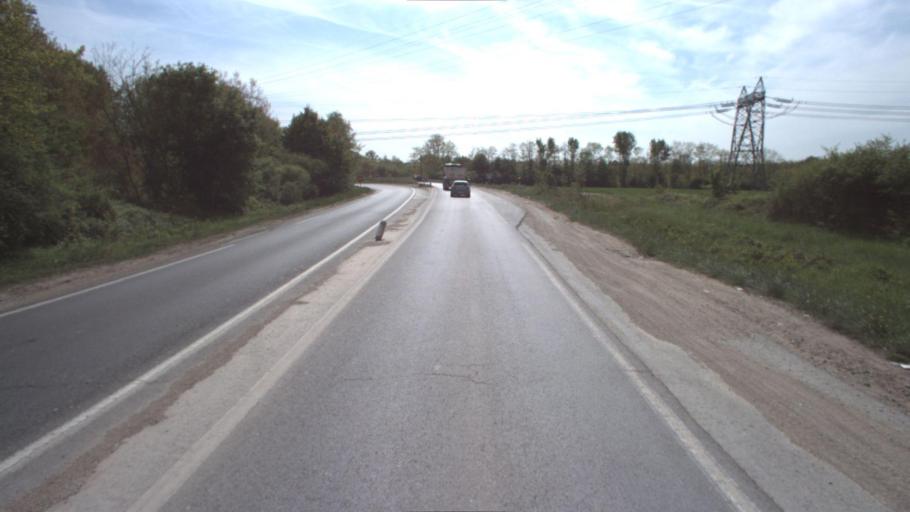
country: FR
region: Ile-de-France
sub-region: Departement de Seine-et-Marne
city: Villevaude
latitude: 48.8991
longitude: 2.6615
